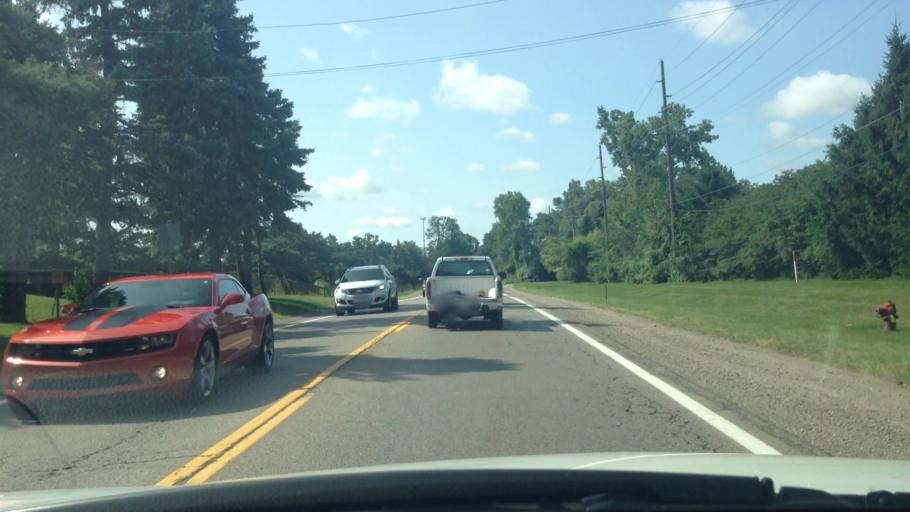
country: US
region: Michigan
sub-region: Oakland County
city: Wolverine Lake
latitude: 42.5830
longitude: -83.4465
